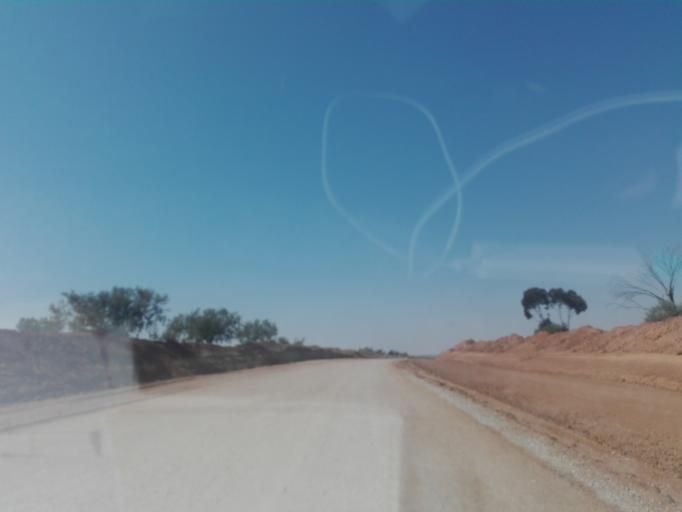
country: TN
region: Safaqis
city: Sfax
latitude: 34.7108
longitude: 10.4982
